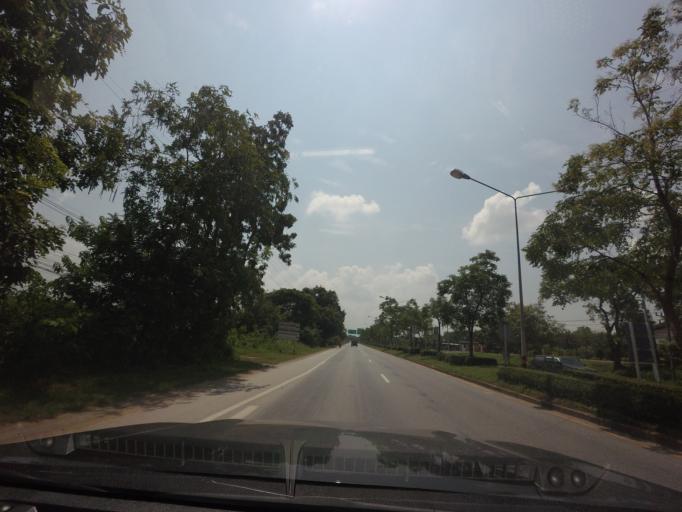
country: TH
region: Uttaradit
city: Uttaradit
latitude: 17.6132
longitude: 100.1236
